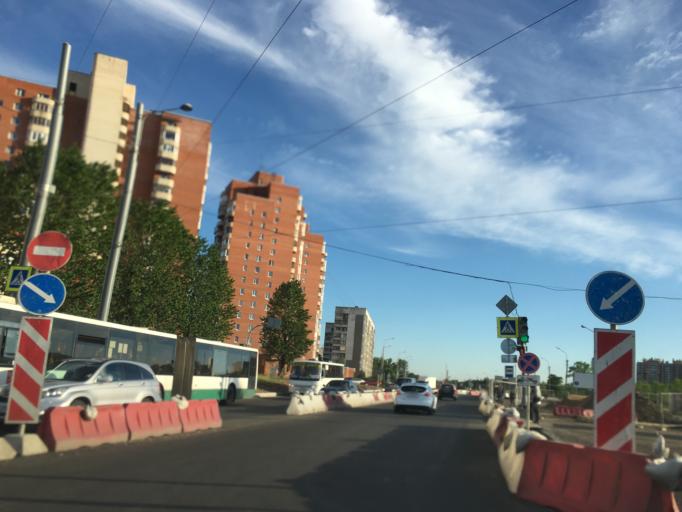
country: RU
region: St.-Petersburg
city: Uritsk
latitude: 59.8329
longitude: 30.1946
